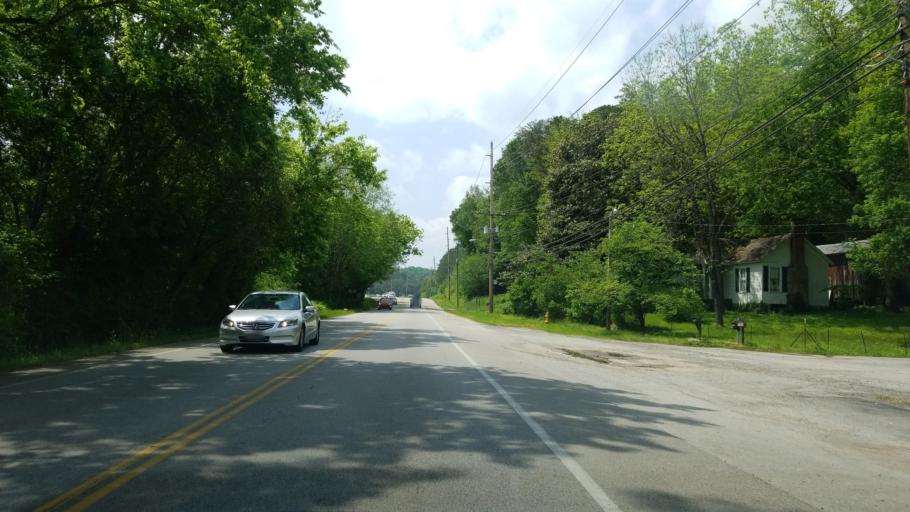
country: US
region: Tennessee
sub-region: Hamilton County
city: Falling Water
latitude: 35.1941
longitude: -85.2447
